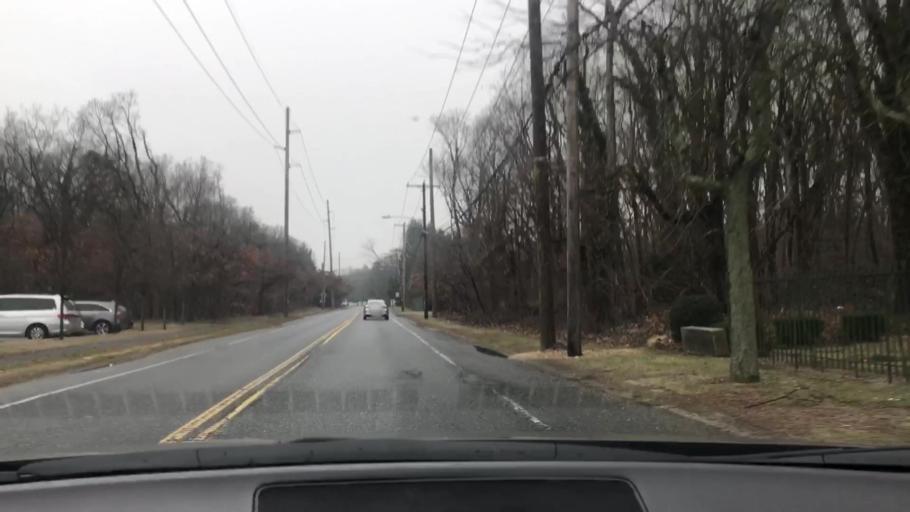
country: US
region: New York
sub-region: Suffolk County
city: South Huntington
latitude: 40.8149
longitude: -73.3801
